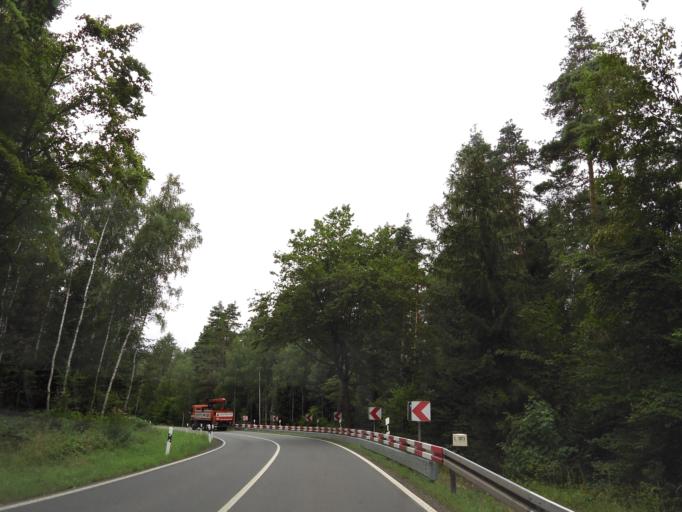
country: DE
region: Thuringia
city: Bad Klosterlausnitz
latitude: 50.9345
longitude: 11.8559
